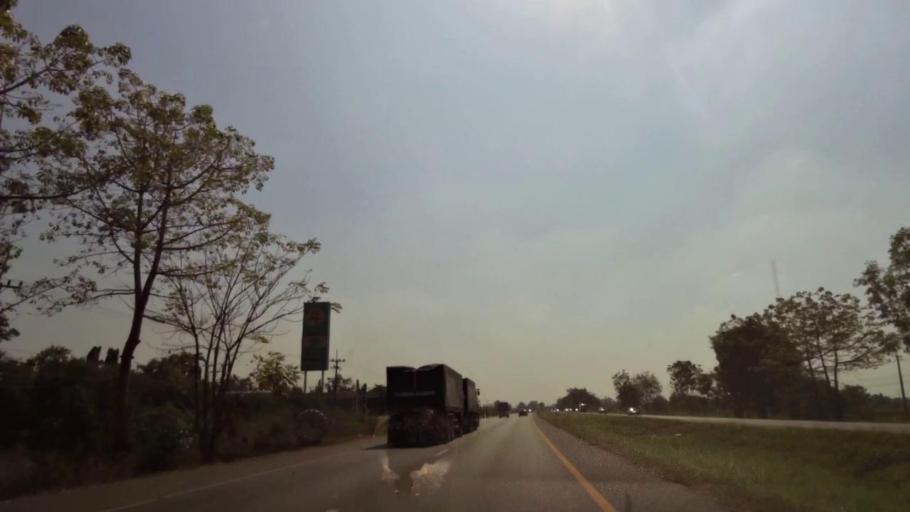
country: TH
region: Phichit
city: Wachira Barami
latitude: 16.4787
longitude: 100.1470
